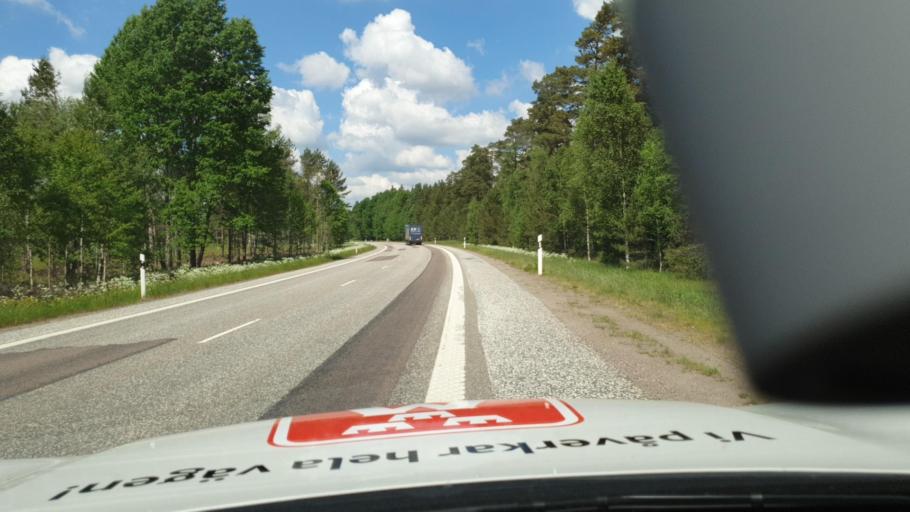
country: SE
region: Joenkoeping
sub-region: Jonkopings Kommun
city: Odensjo
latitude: 57.6400
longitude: 14.2041
